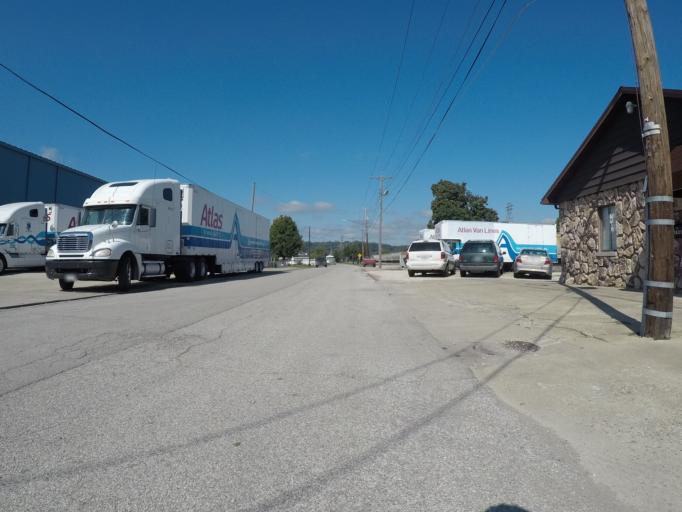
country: US
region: West Virginia
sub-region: Wayne County
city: Kenova
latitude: 38.4037
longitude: -82.5794
